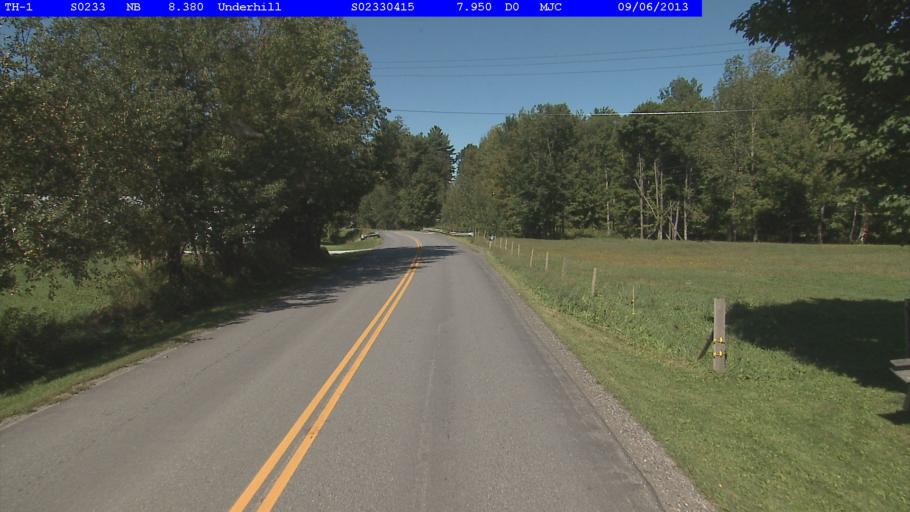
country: US
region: Vermont
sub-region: Chittenden County
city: Jericho
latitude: 44.5792
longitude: -72.8627
